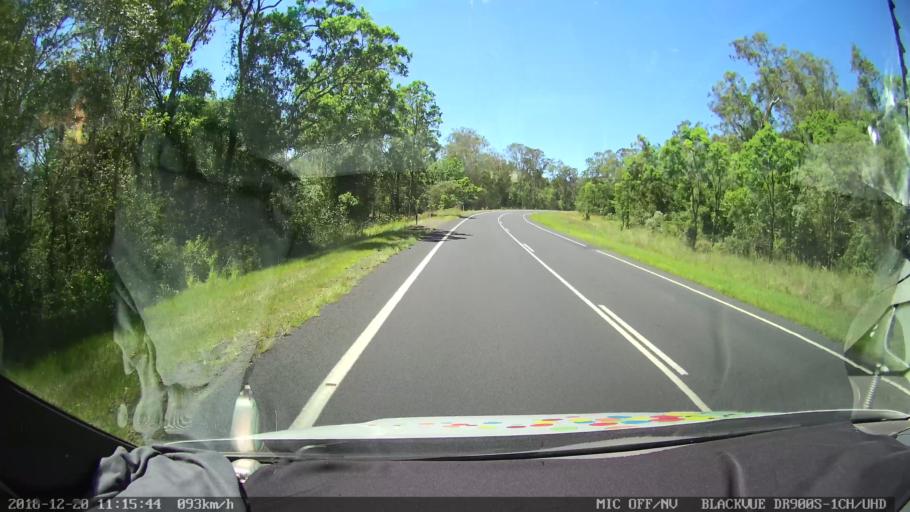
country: AU
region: New South Wales
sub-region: Richmond Valley
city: Casino
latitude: -29.0169
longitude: 153.0105
